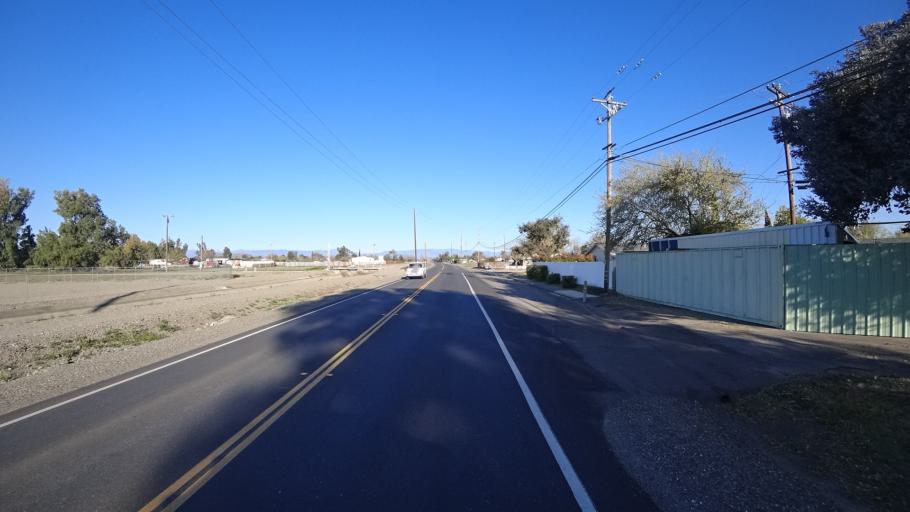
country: US
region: California
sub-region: Glenn County
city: Orland
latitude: 39.7584
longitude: -122.2241
